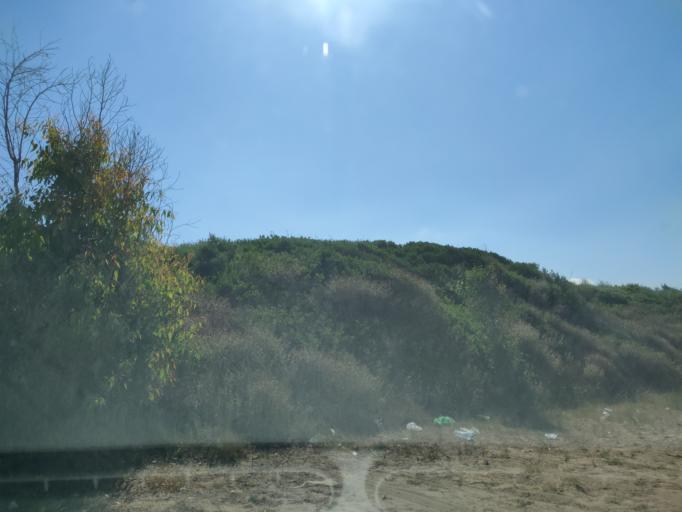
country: IT
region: Latium
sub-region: Citta metropolitana di Roma Capitale
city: Aurelia
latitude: 42.1716
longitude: 11.7408
